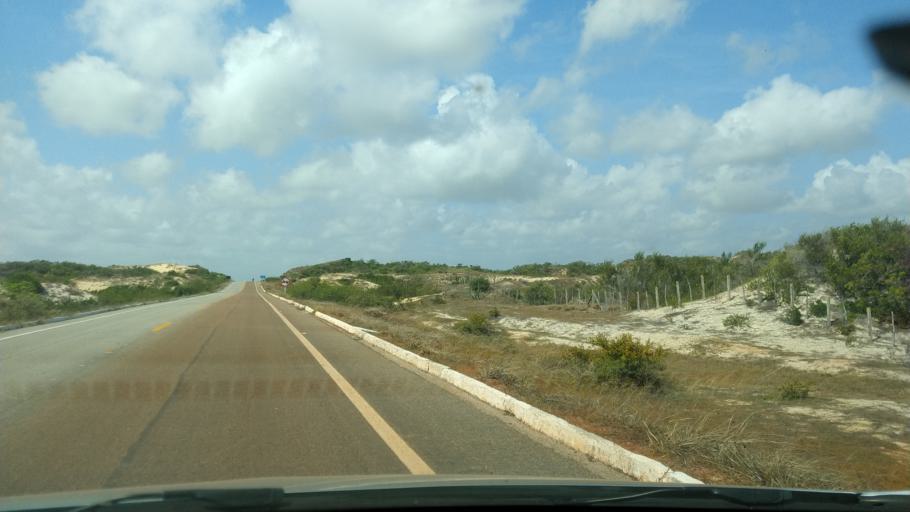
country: BR
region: Rio Grande do Norte
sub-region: Touros
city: Touros
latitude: -5.1602
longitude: -35.5013
